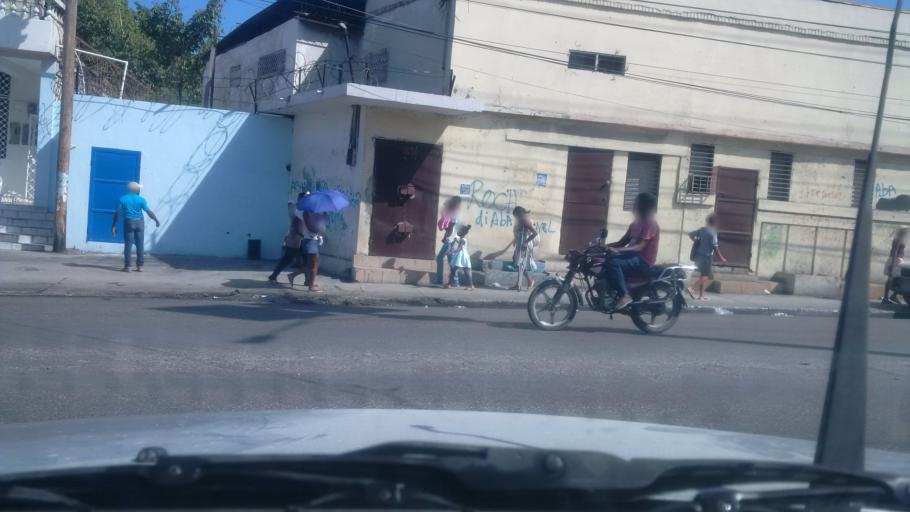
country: HT
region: Ouest
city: Delmas 73
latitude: 18.5330
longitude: -72.2908
